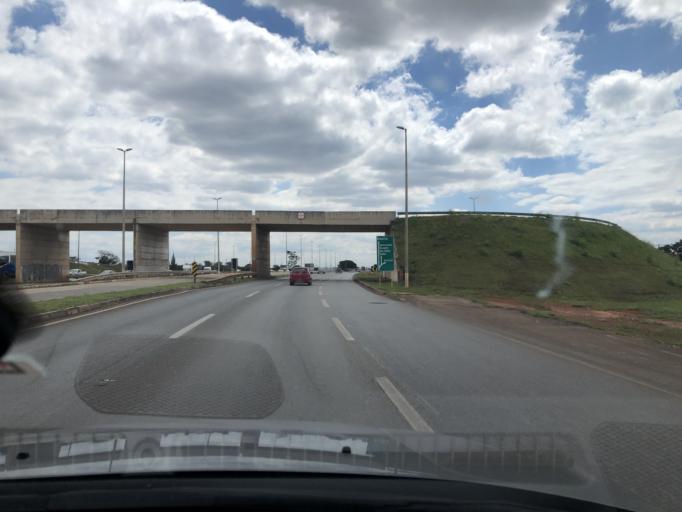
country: BR
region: Federal District
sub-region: Brasilia
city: Brasilia
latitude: -15.9817
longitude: -47.9885
